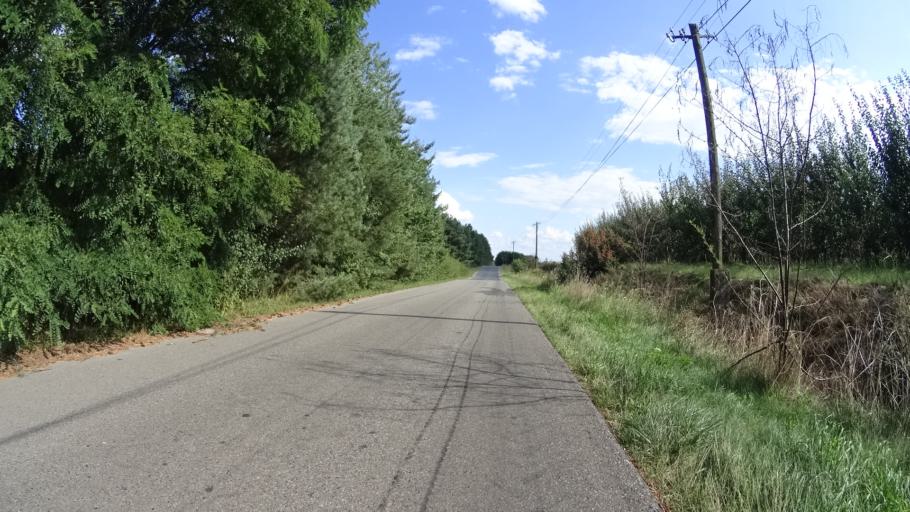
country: PL
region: Masovian Voivodeship
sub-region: Powiat grojecki
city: Mogielnica
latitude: 51.6871
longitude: 20.7531
